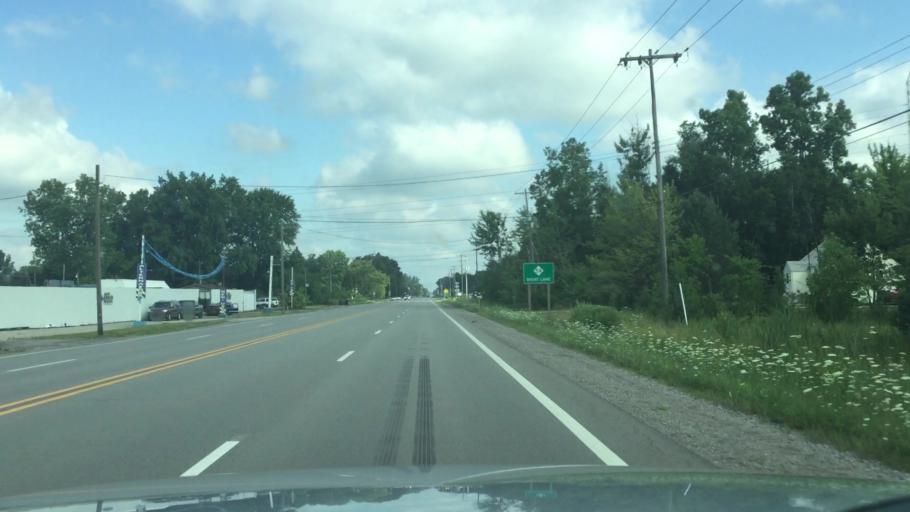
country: US
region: Michigan
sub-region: Genesee County
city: Clio
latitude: 43.2008
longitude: -83.7320
